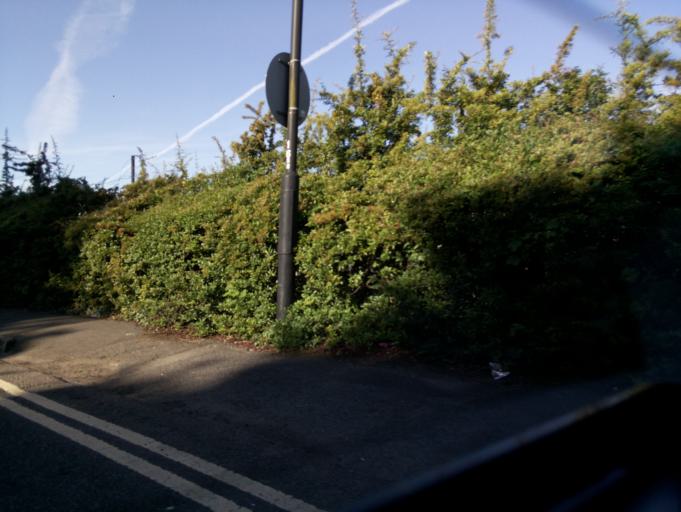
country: GB
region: England
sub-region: Bristol
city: Bristol
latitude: 51.4487
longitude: -2.5572
